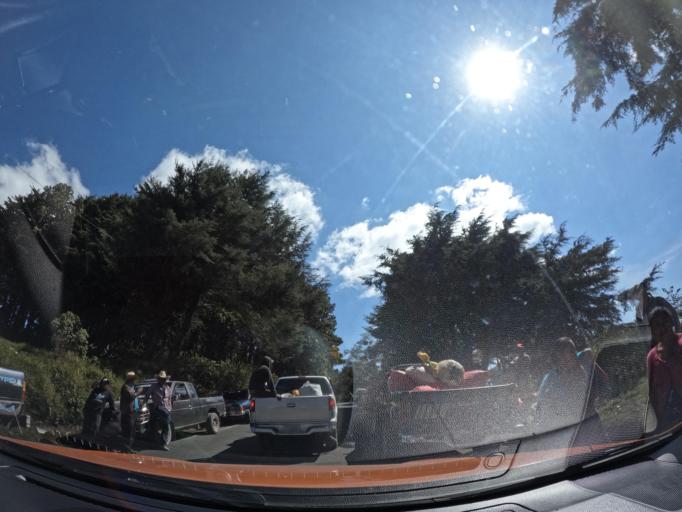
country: GT
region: Chimaltenango
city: Patzun
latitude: 14.6516
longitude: -91.0472
